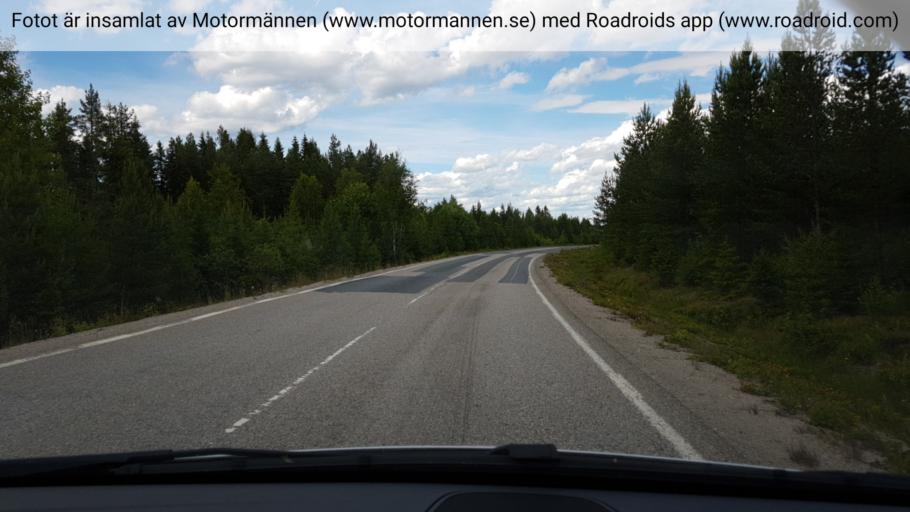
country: SE
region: Jaemtland
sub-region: Braecke Kommun
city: Braecke
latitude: 62.3917
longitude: 15.2283
